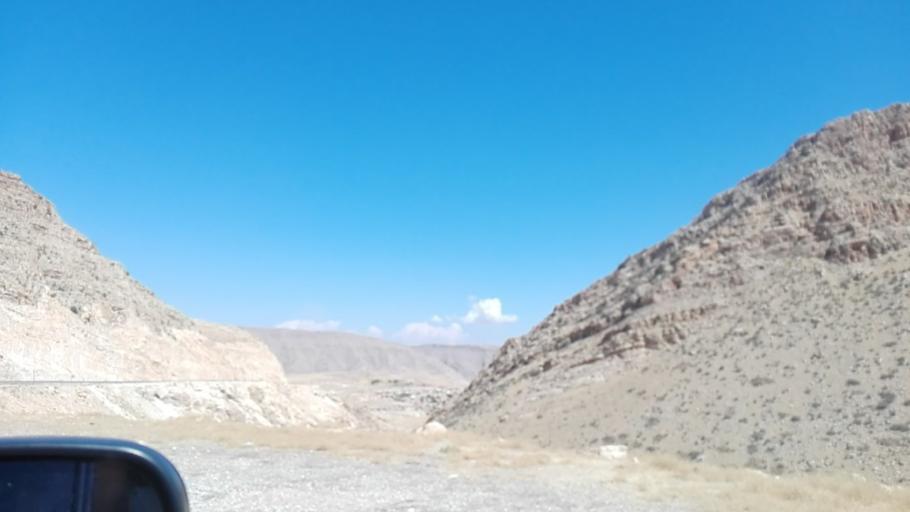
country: TR
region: Batman
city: Hasankeyf
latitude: 37.6966
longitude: 41.4585
